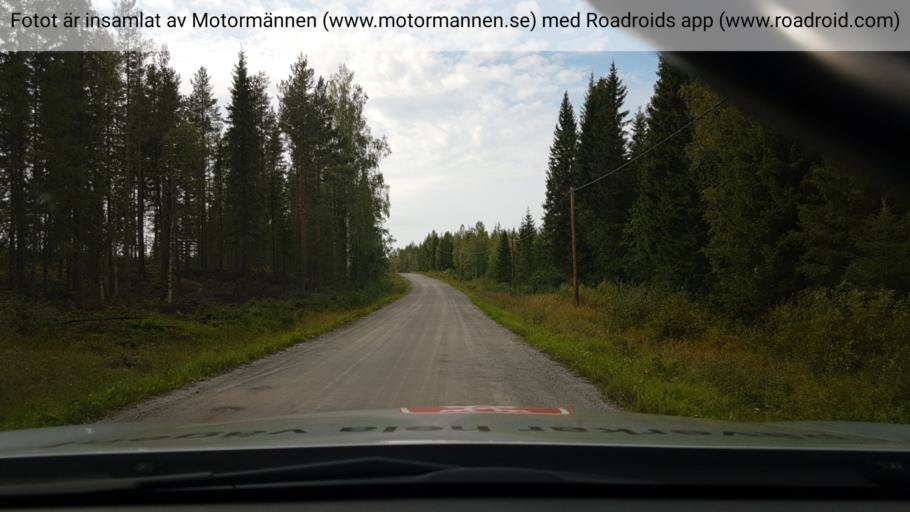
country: SE
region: Vaesterbotten
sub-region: Vannas Kommun
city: Vaennaes
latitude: 63.8726
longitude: 19.5518
